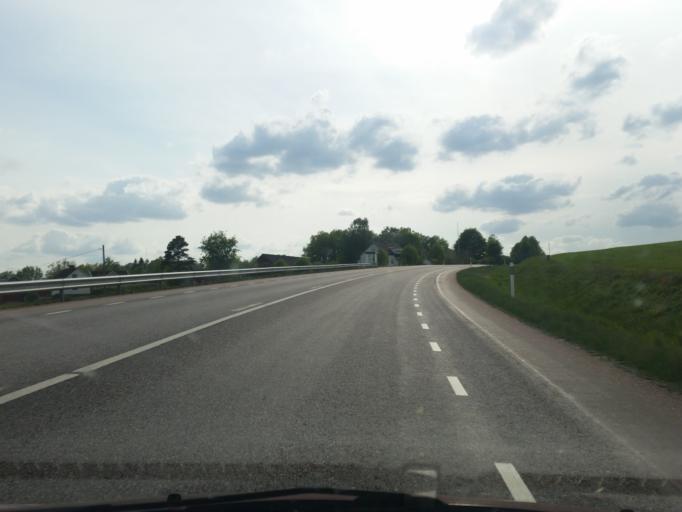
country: SE
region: Vaestra Goetaland
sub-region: Ulricehamns Kommun
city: Ulricehamn
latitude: 57.8100
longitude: 13.2730
